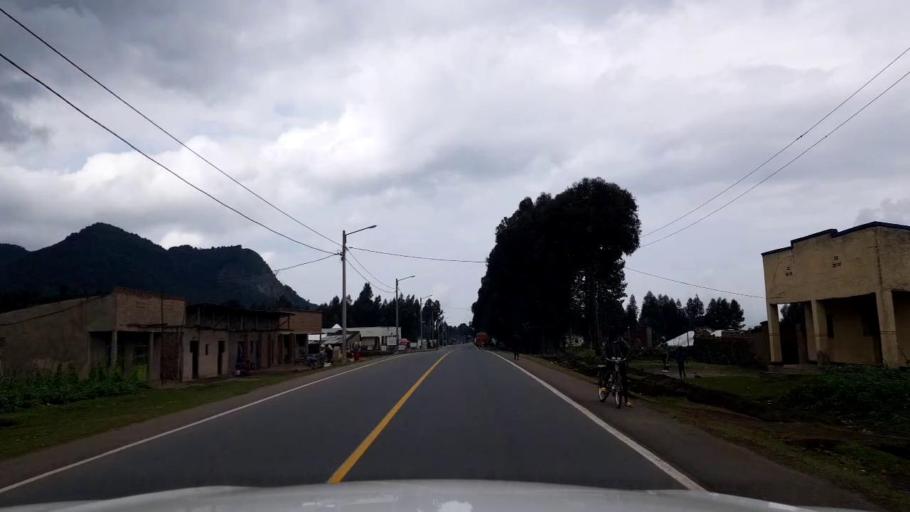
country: RW
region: Western Province
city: Gisenyi
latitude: -1.6361
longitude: 29.4066
